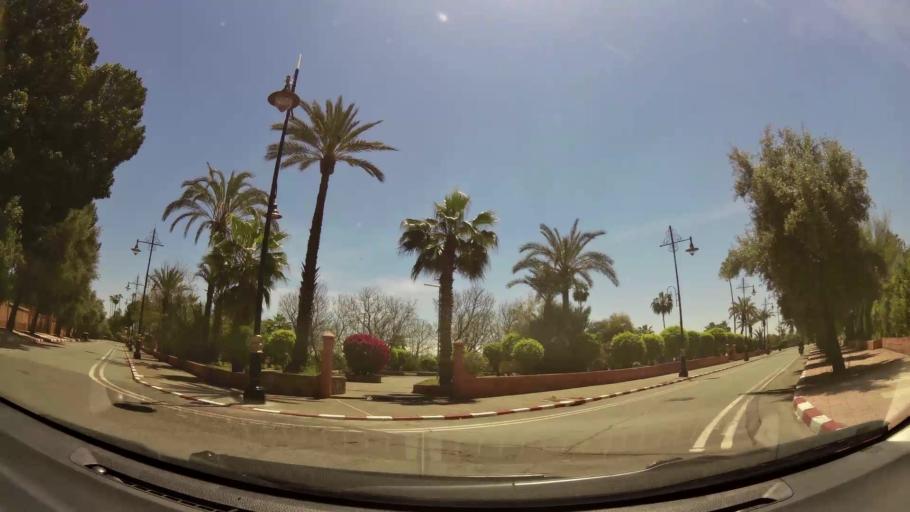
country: MA
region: Marrakech-Tensift-Al Haouz
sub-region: Marrakech
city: Marrakesh
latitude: 31.6198
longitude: -8.0060
